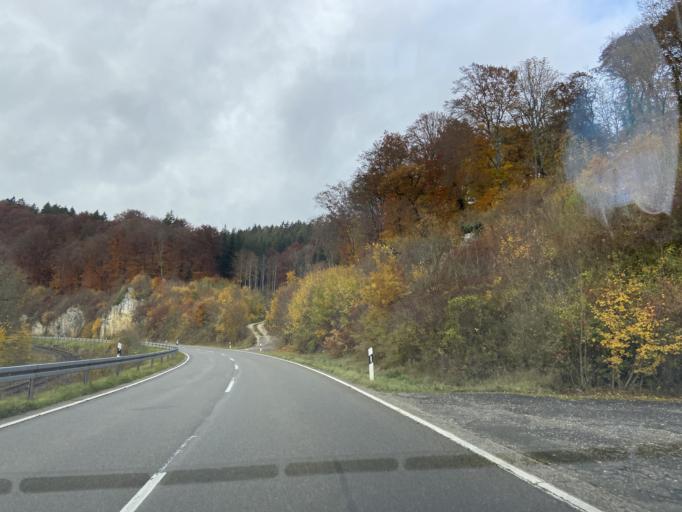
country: DE
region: Baden-Wuerttemberg
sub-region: Tuebingen Region
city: Inzigkofen
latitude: 48.0813
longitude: 9.1722
